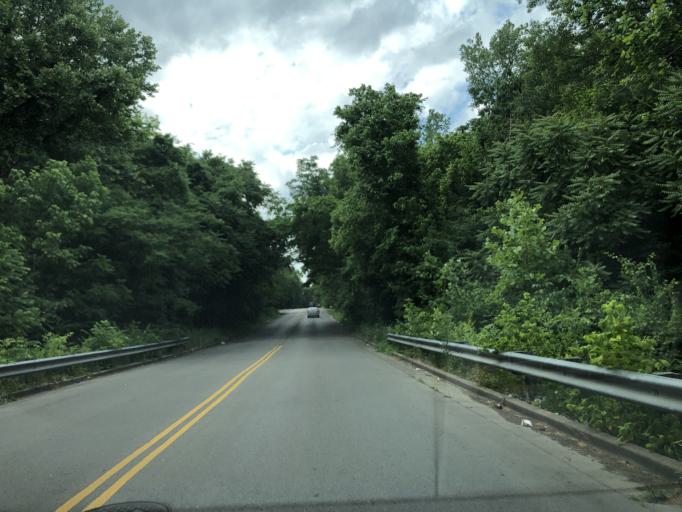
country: US
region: Tennessee
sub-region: Davidson County
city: Lakewood
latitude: 36.2666
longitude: -86.6813
